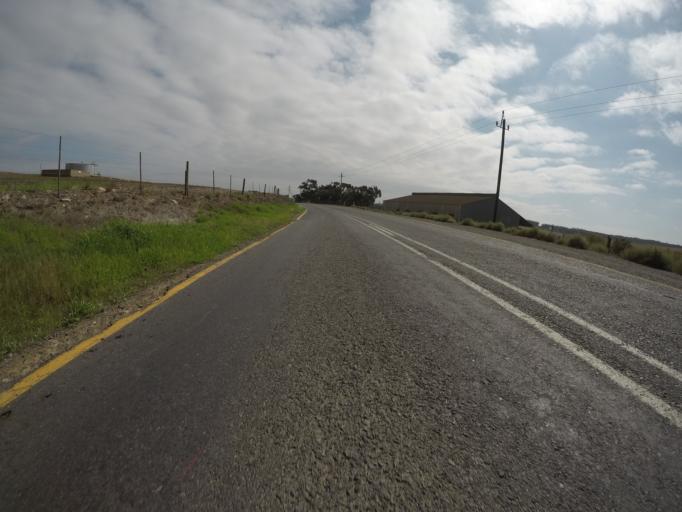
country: ZA
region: Western Cape
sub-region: City of Cape Town
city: Sunset Beach
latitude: -33.7814
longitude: 18.5591
